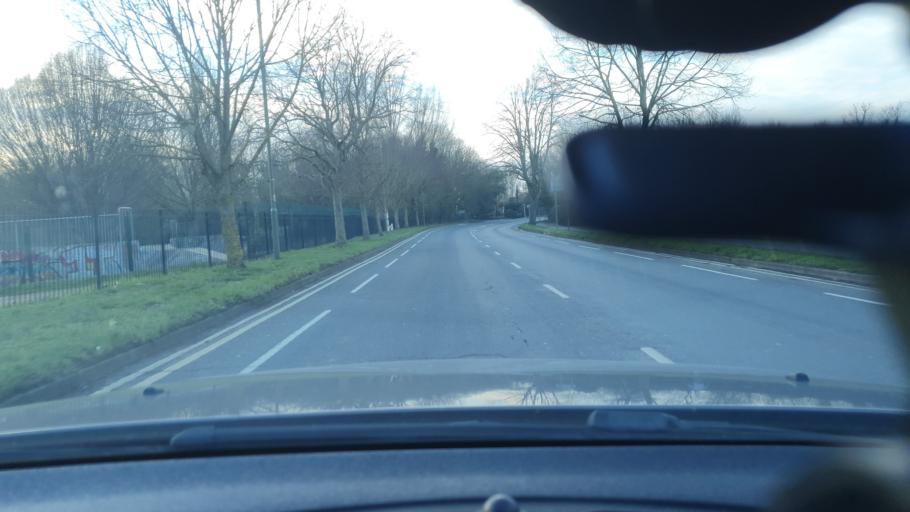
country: GB
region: England
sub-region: Surrey
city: Staines
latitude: 51.4376
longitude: -0.5231
